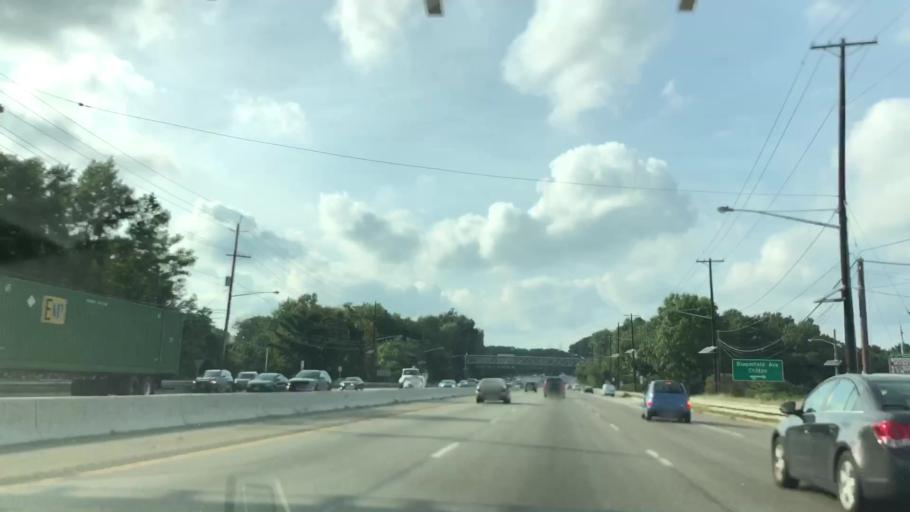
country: US
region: New Jersey
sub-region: Essex County
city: Nutley
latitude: 40.8396
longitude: -74.1590
